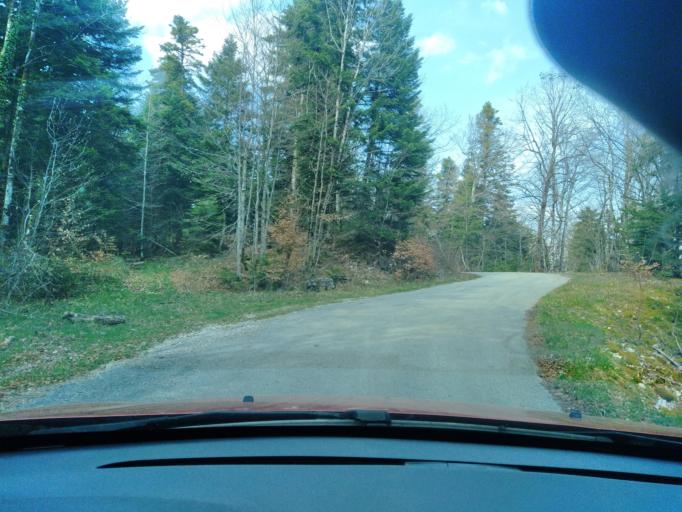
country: FR
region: Franche-Comte
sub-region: Departement du Jura
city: Moirans-en-Montagne
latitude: 46.4721
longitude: 5.7629
